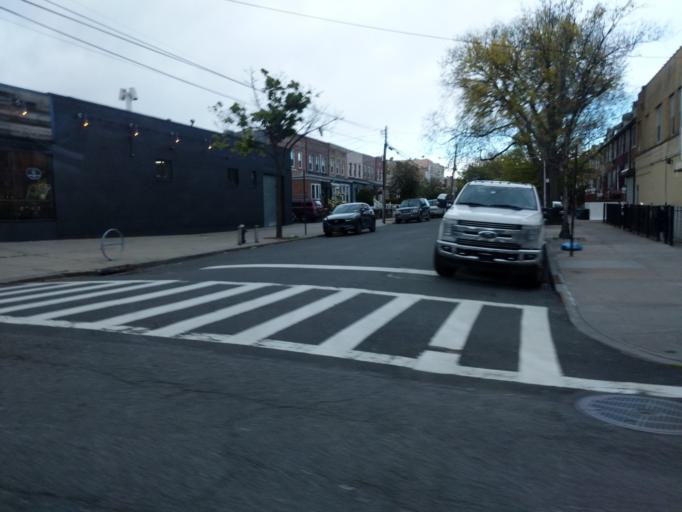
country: US
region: New York
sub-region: Queens County
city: Long Island City
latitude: 40.7708
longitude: -73.9031
